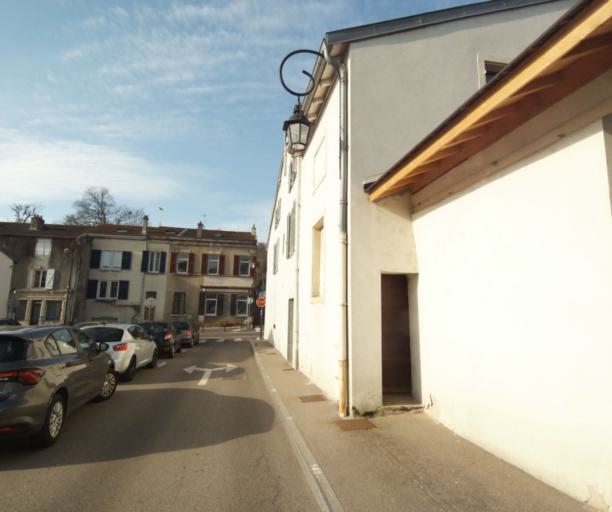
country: FR
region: Lorraine
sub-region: Departement de Meurthe-et-Moselle
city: Laxou
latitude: 48.6857
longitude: 6.1414
